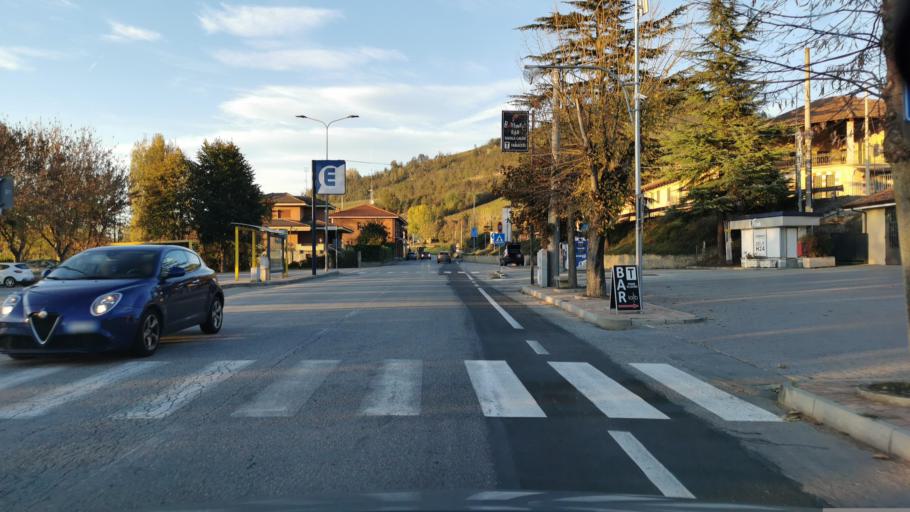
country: IT
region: Piedmont
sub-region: Provincia di Cuneo
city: Monchiero Borgonuovo
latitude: 44.5726
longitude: 7.9170
